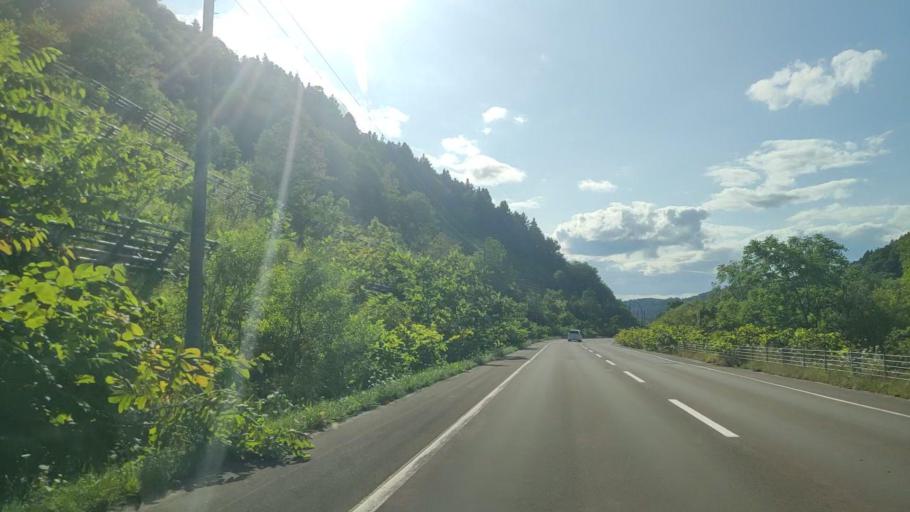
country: JP
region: Hokkaido
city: Nayoro
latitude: 44.7299
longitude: 142.1001
